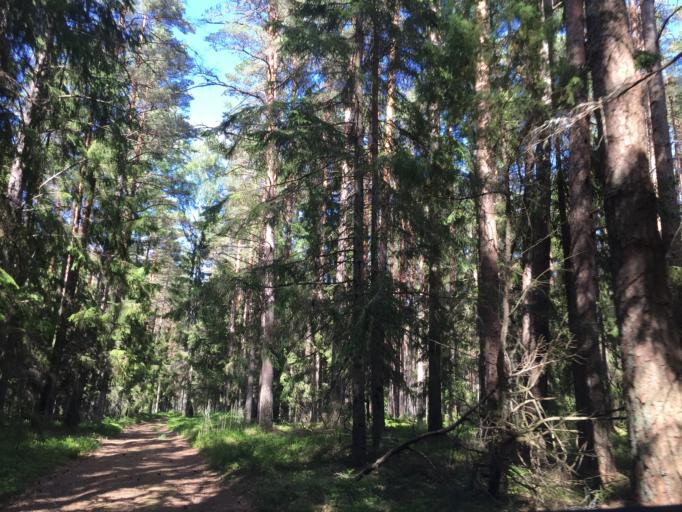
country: LV
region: Ventspils
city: Ventspils
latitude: 57.4749
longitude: 21.6580
